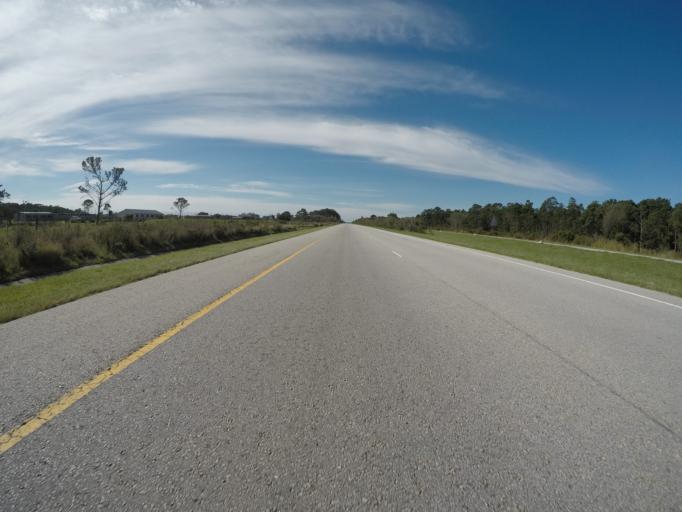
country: ZA
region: Eastern Cape
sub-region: Nelson Mandela Bay Metropolitan Municipality
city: Uitenhage
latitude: -33.9209
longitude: 25.3018
